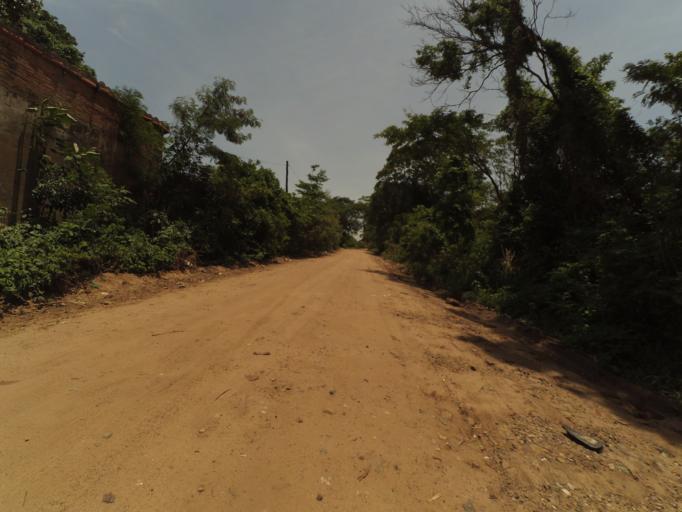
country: BO
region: Santa Cruz
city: Santa Cruz de la Sierra
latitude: -17.8262
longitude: -63.2527
